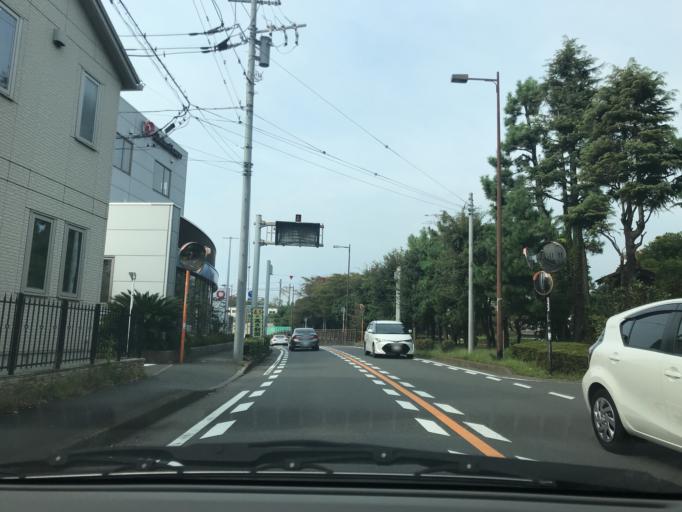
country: JP
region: Kanagawa
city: Fujisawa
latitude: 35.3366
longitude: 139.4691
